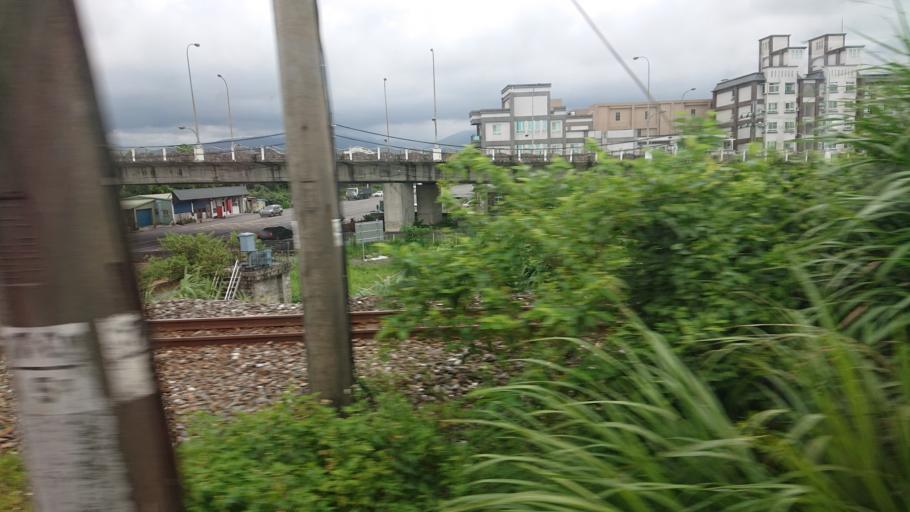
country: TW
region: Taiwan
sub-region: Yilan
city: Yilan
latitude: 24.7646
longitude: 121.7622
